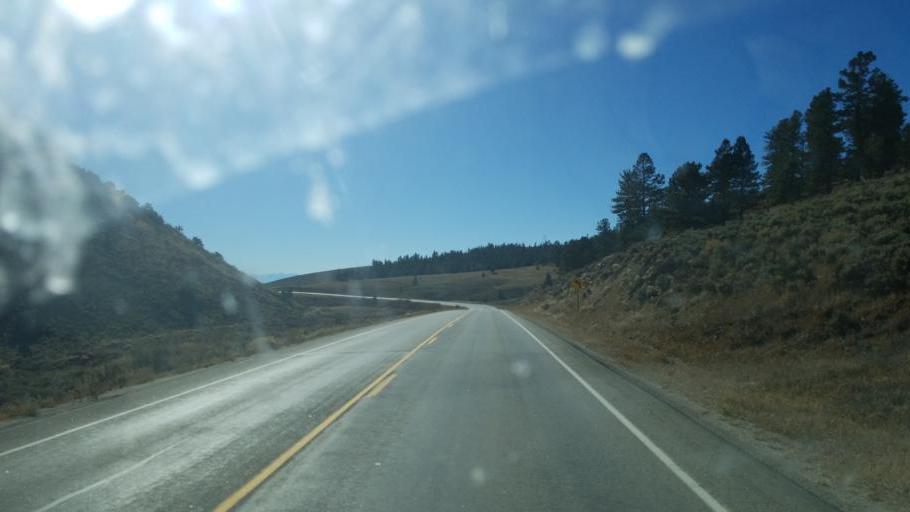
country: US
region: Colorado
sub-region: Chaffee County
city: Salida
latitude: 38.4003
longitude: -106.0662
